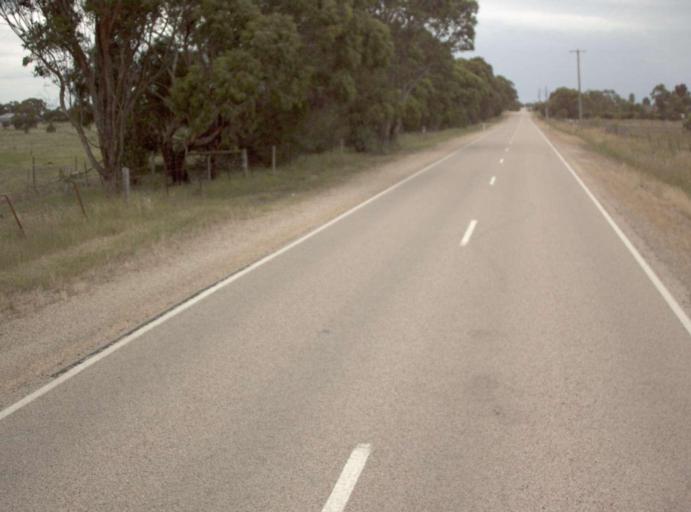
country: AU
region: Victoria
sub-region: East Gippsland
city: Bairnsdale
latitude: -37.8599
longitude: 147.5635
